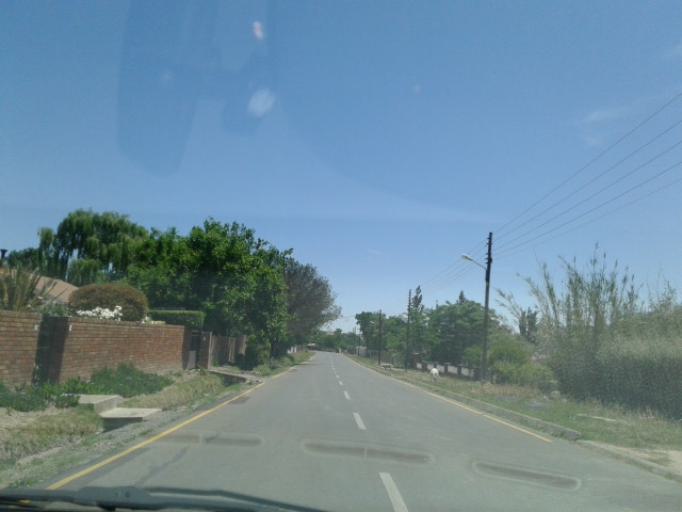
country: LS
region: Maseru
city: Maseru
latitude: -29.3024
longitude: 27.4750
